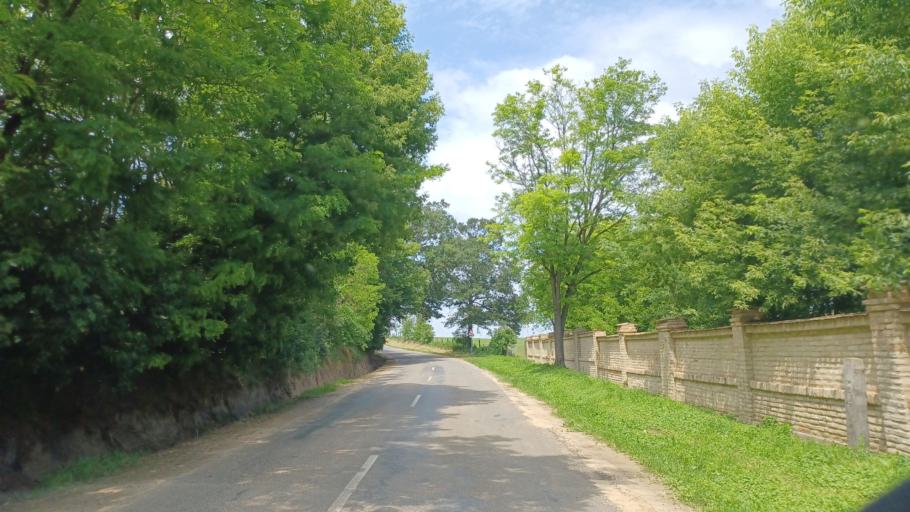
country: HU
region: Tolna
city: Simontornya
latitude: 46.6988
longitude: 18.5167
